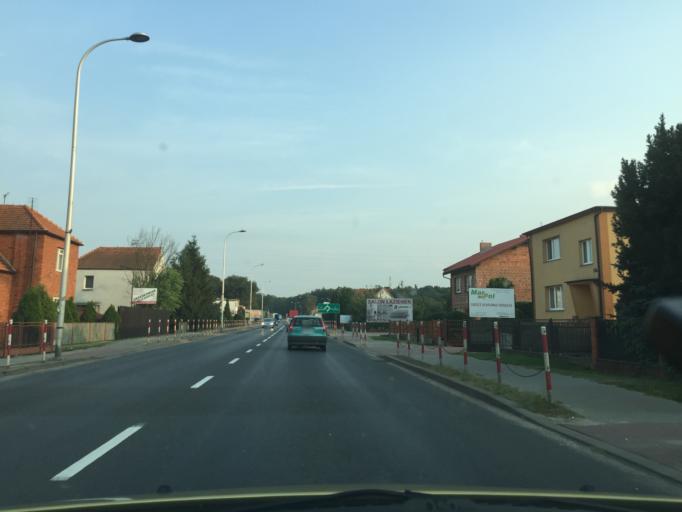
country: PL
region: Greater Poland Voivodeship
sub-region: Powiat jarocinski
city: Jarocin
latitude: 51.9582
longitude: 17.5167
